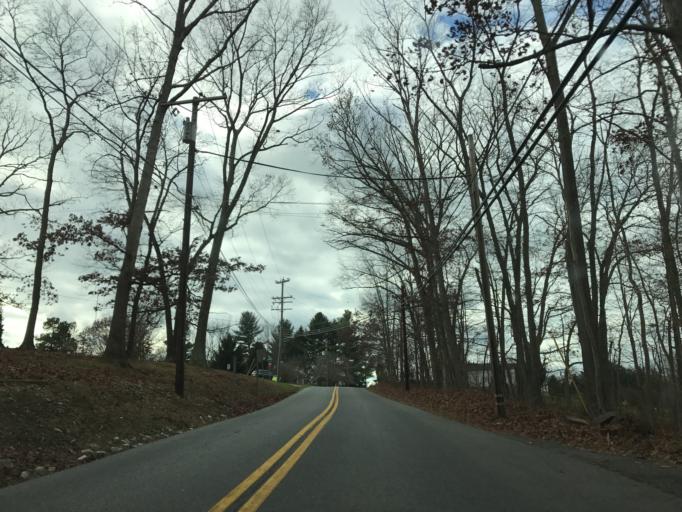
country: US
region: Pennsylvania
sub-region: York County
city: New Freedom
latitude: 39.6254
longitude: -76.6482
